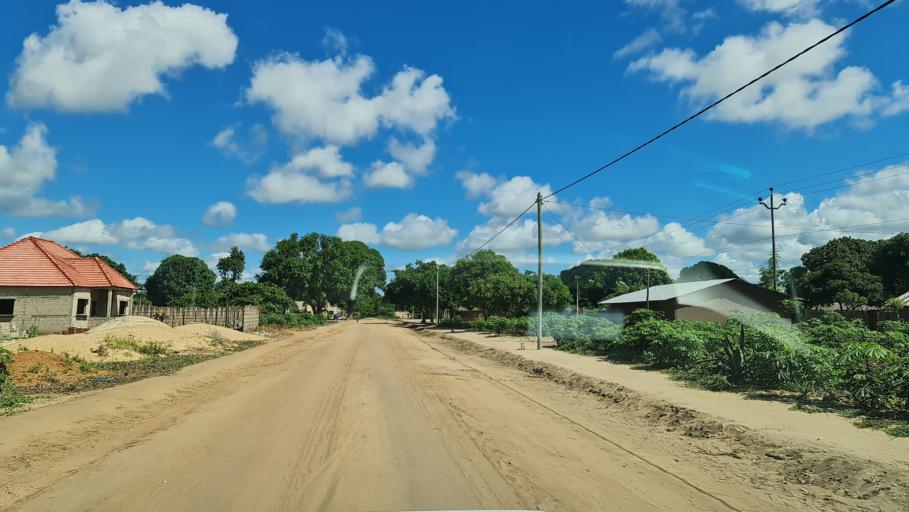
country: MZ
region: Nampula
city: Ilha de Mocambique
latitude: -15.5531
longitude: 40.4085
